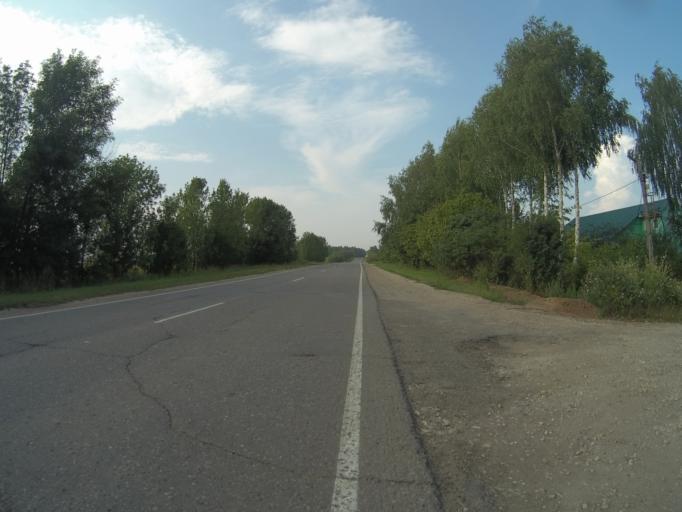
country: RU
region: Vladimir
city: Suzdal'
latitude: 56.4140
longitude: 40.4285
